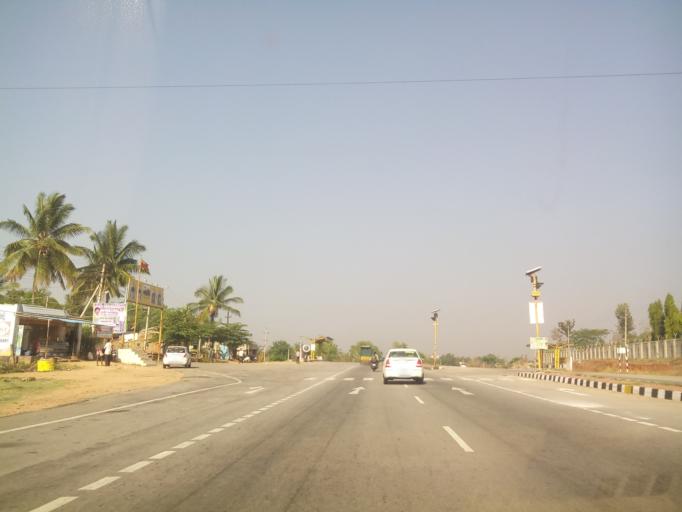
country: IN
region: Karnataka
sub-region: Bangalore Rural
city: Nelamangala
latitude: 13.0619
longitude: 77.2974
